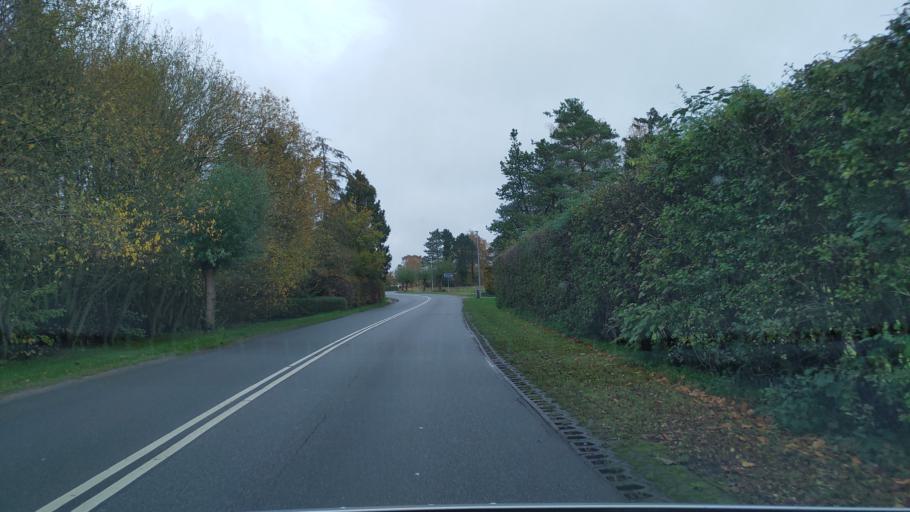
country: DK
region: Capital Region
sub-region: Tarnby Kommune
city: Tarnby
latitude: 55.6047
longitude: 12.6057
